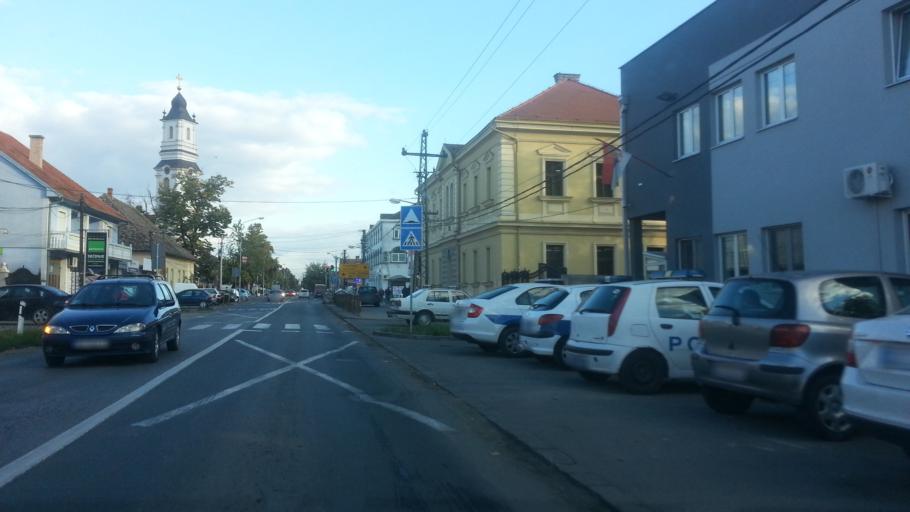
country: RS
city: Novi Banovci
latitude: 44.9069
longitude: 20.2733
